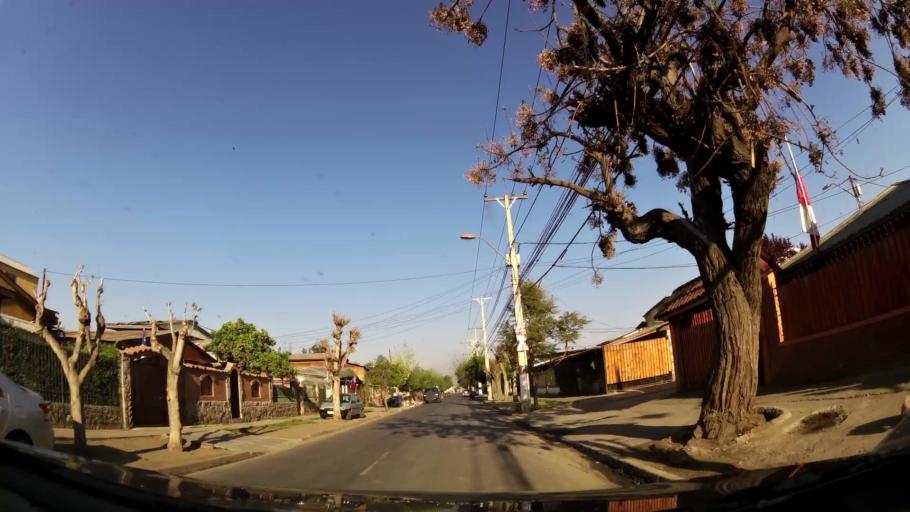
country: CL
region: Santiago Metropolitan
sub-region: Provincia de Santiago
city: Santiago
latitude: -33.3787
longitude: -70.6328
